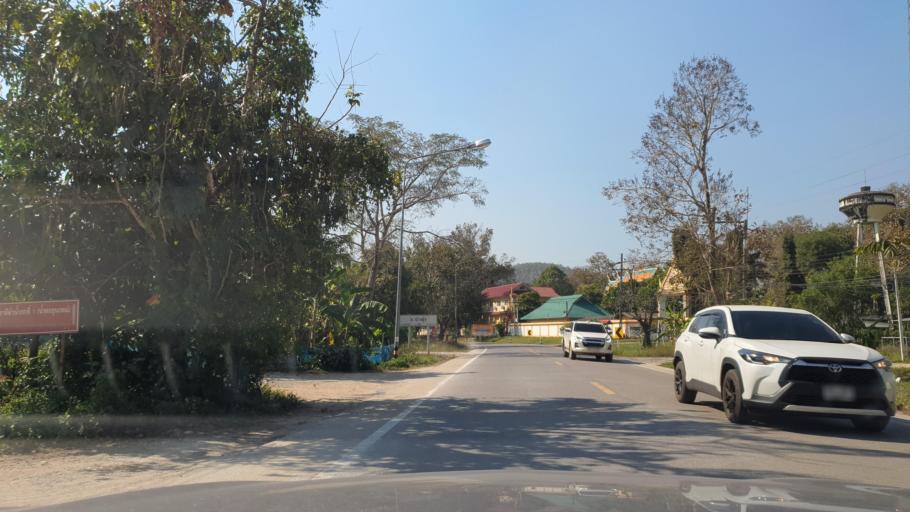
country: TH
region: Chiang Rai
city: Mae Lao
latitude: 19.8336
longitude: 99.7009
